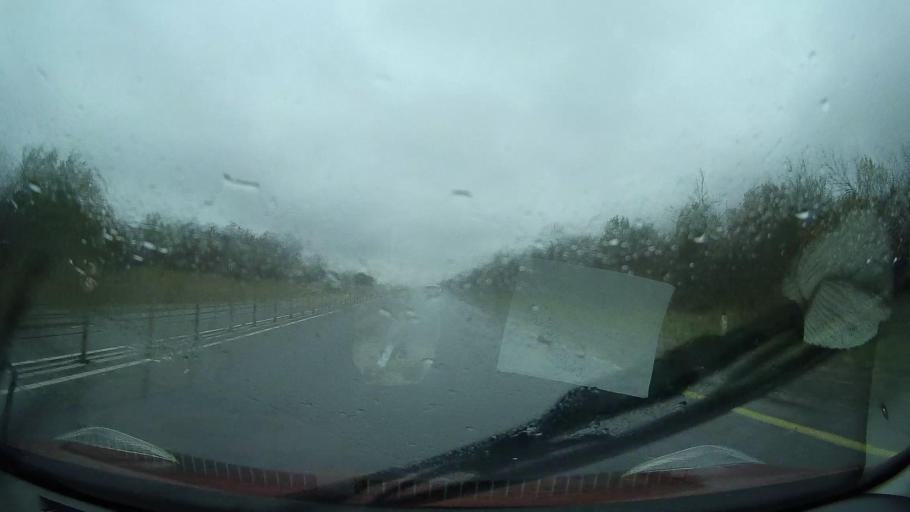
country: RU
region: Stavropol'skiy
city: Nevinnomyssk
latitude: 44.6387
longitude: 41.9803
